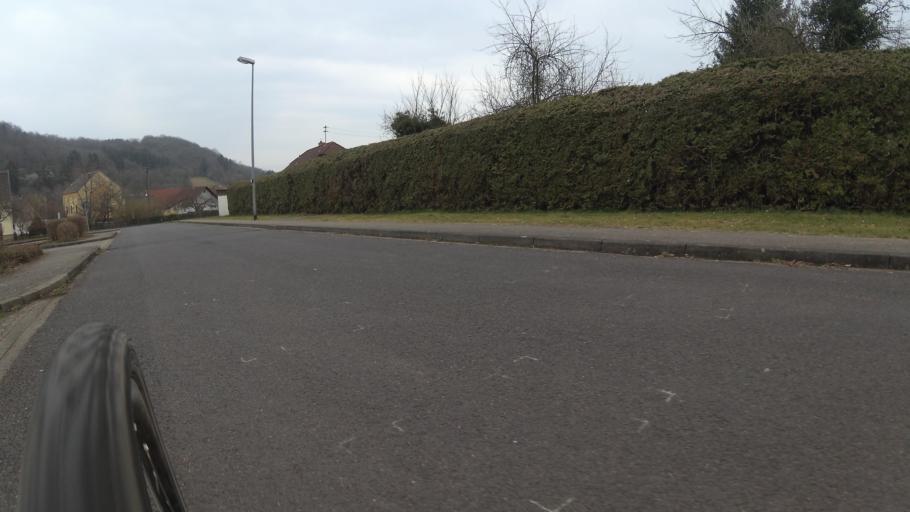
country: DE
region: Rheinland-Pfalz
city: Hoppstadten-Weiersbach
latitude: 49.6193
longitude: 7.1942
